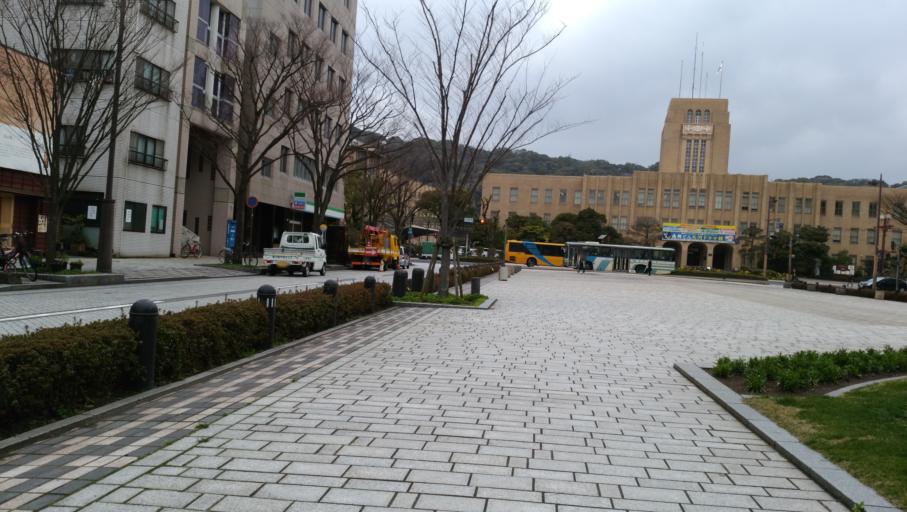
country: JP
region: Kagoshima
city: Kagoshima-shi
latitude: 31.5961
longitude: 130.5587
